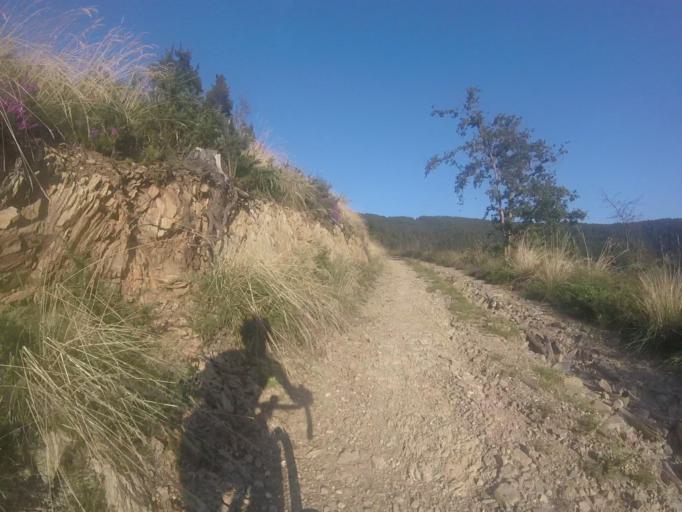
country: ES
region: Navarre
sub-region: Provincia de Navarra
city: Arano
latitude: 43.2502
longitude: -1.8576
